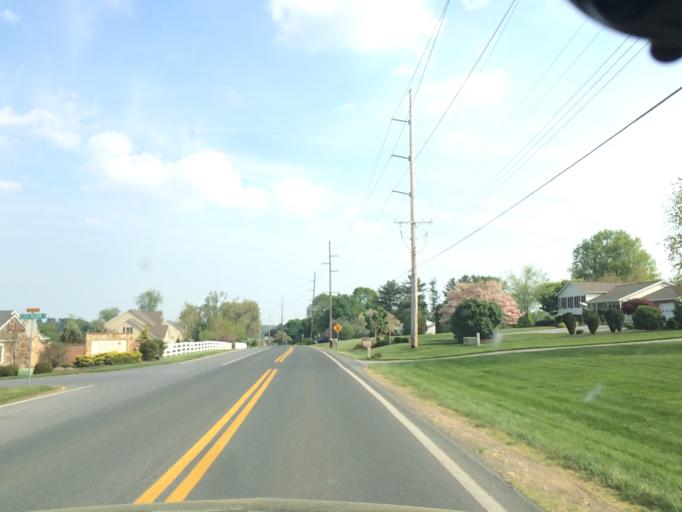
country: US
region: Maryland
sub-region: Carroll County
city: Eldersburg
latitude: 39.4760
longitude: -76.9129
